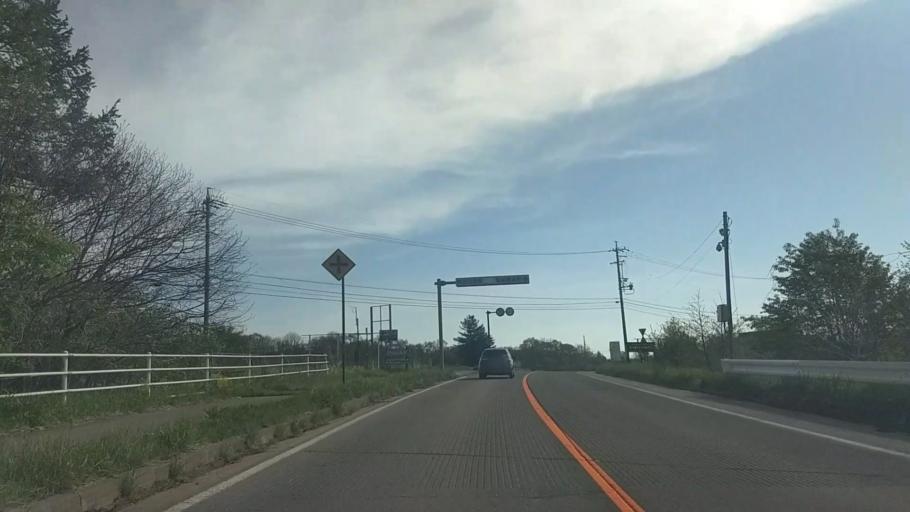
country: JP
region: Yamanashi
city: Nirasaki
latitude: 35.9445
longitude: 138.4517
